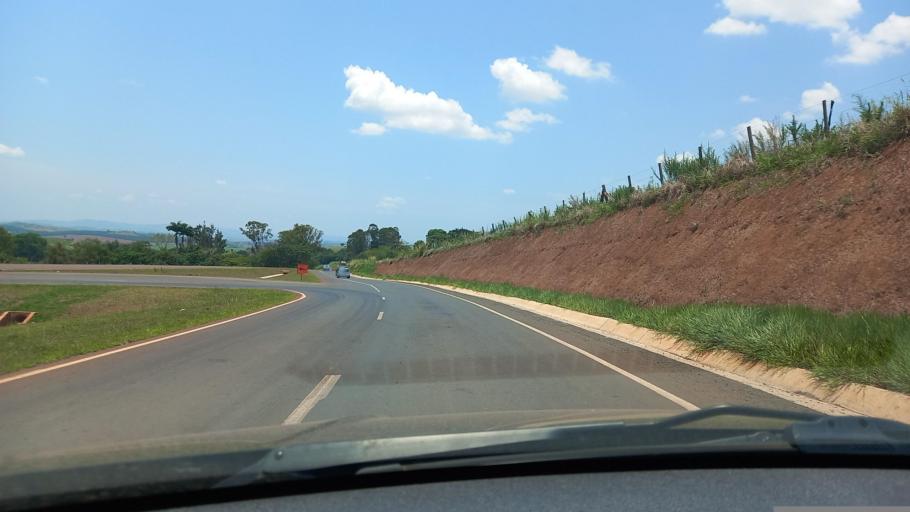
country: BR
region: Sao Paulo
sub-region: Moji-Guacu
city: Mogi-Gaucu
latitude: -22.3394
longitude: -46.8822
